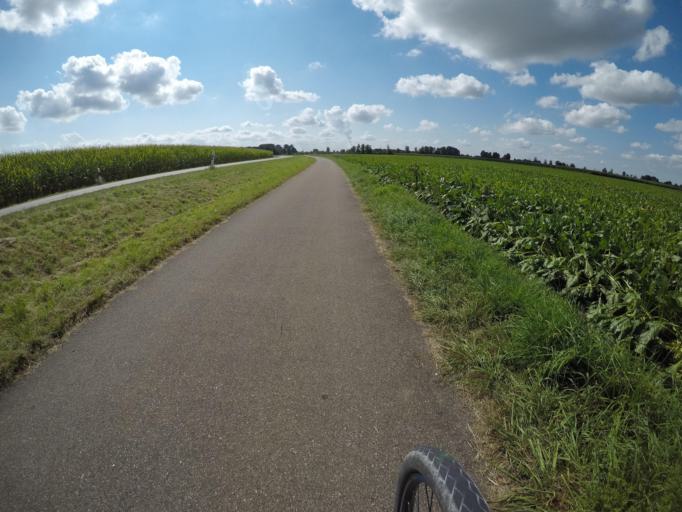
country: DE
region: Bavaria
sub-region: Swabia
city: Finningen
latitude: 48.6189
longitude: 10.5046
